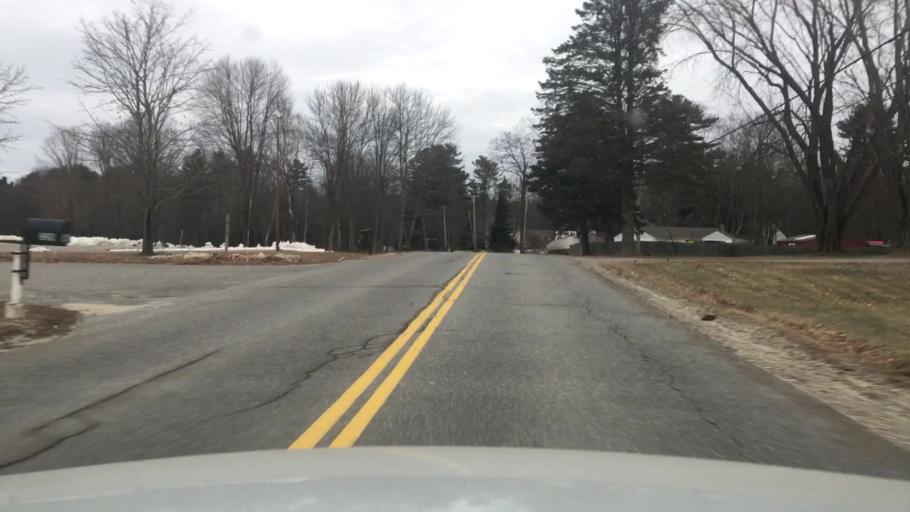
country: US
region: Maine
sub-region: Cumberland County
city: Brunswick
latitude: 43.8939
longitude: -70.0030
